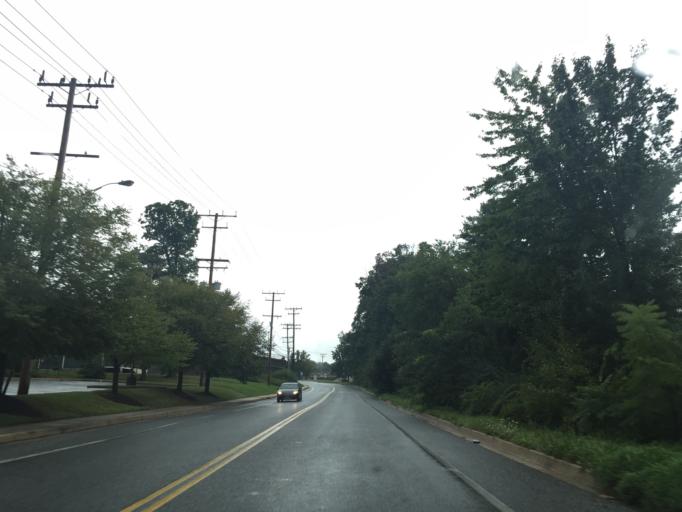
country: US
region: Maryland
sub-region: Harford County
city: Bel Air South
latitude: 39.4763
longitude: -76.3077
